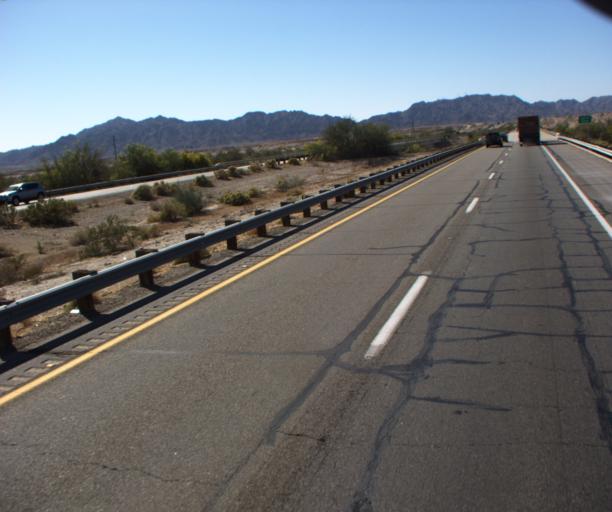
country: US
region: Arizona
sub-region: Yuma County
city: Wellton
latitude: 32.6592
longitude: -114.2511
